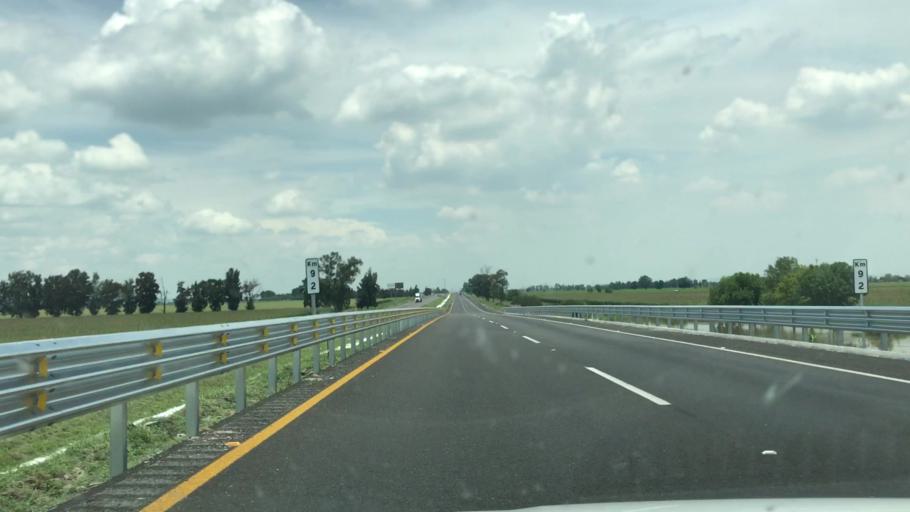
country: MX
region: Guanajuato
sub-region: Salamanca
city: San Vicente de Flores
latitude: 20.6354
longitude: -101.2577
